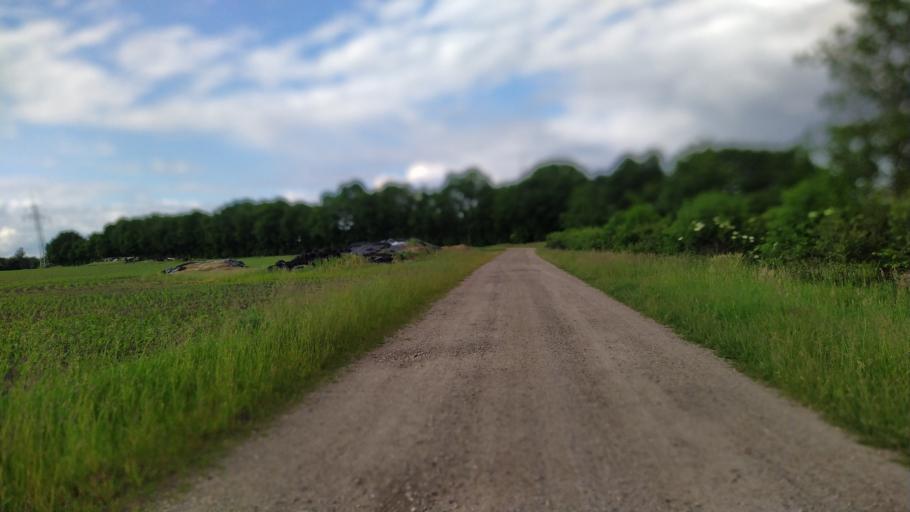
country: DE
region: Lower Saxony
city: Sandbostel
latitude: 53.4321
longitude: 9.1720
